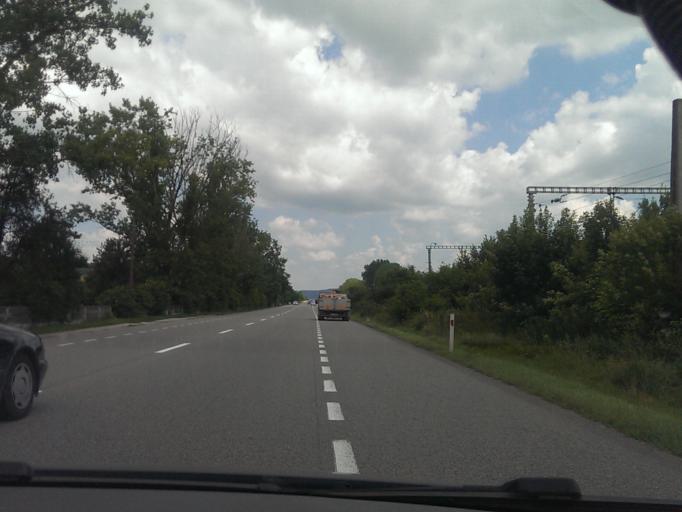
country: RO
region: Cluj
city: Jucu Herghelia
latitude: 46.8659
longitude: 23.7655
